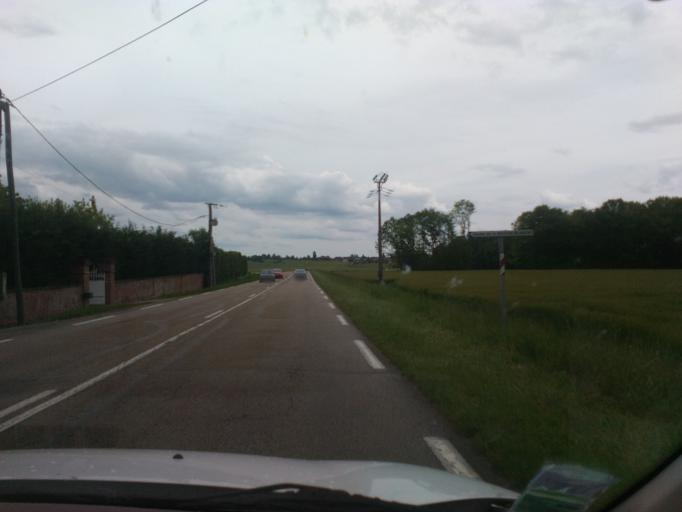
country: FR
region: Champagne-Ardenne
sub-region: Departement de l'Aube
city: Lusigny-sur-Barse
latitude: 48.2420
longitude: 4.3650
